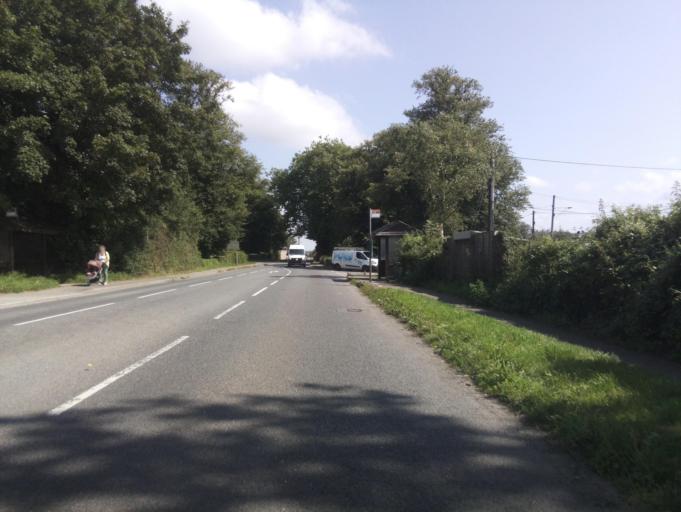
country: GB
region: England
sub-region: Devon
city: Yealmpton
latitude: 50.3468
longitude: -4.0091
